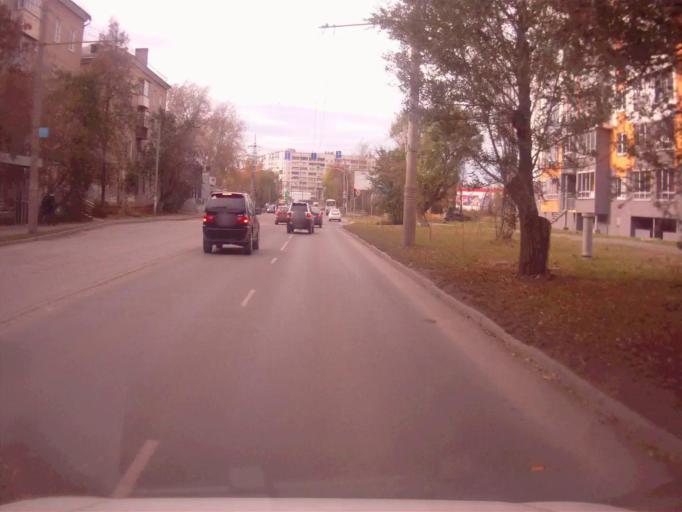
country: RU
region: Chelyabinsk
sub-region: Gorod Chelyabinsk
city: Chelyabinsk
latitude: 55.1158
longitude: 61.4474
